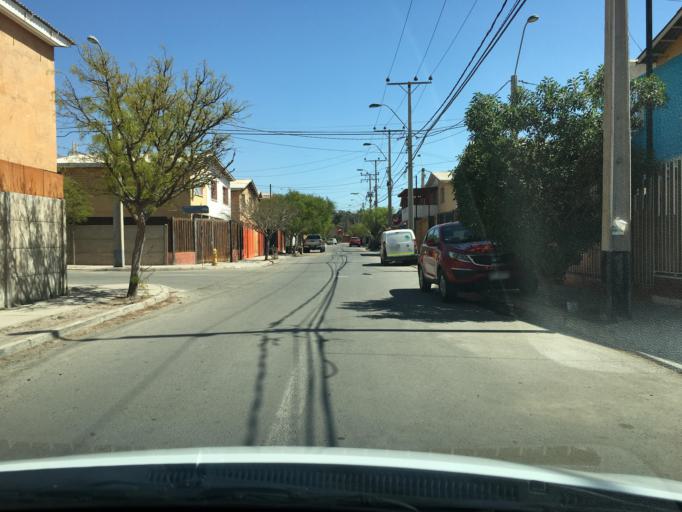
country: CL
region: Atacama
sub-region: Provincia de Copiapo
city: Copiapo
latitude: -27.4093
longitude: -70.2822
